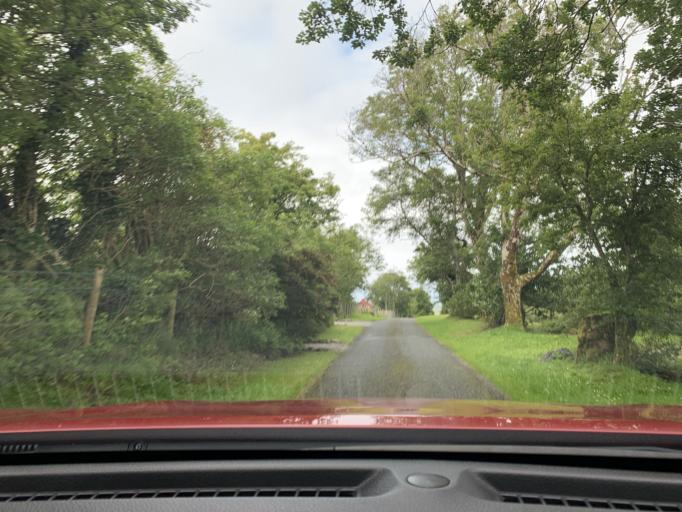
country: IE
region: Connaught
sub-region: Sligo
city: Sligo
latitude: 54.3902
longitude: -8.4059
